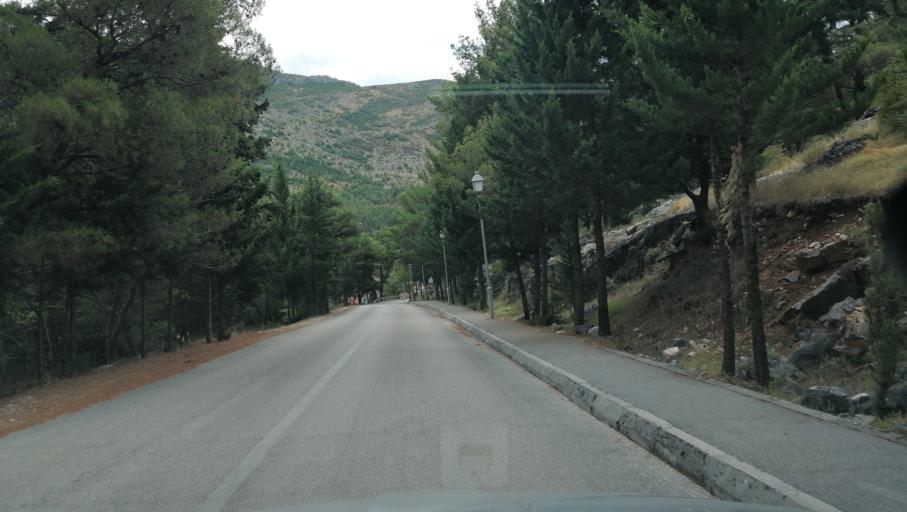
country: BA
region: Republika Srpska
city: Trebinje
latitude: 42.7098
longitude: 18.3621
